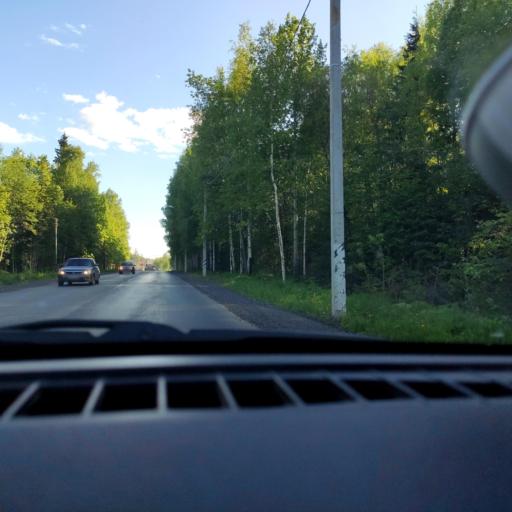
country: RU
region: Perm
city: Perm
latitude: 58.1301
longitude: 56.2992
